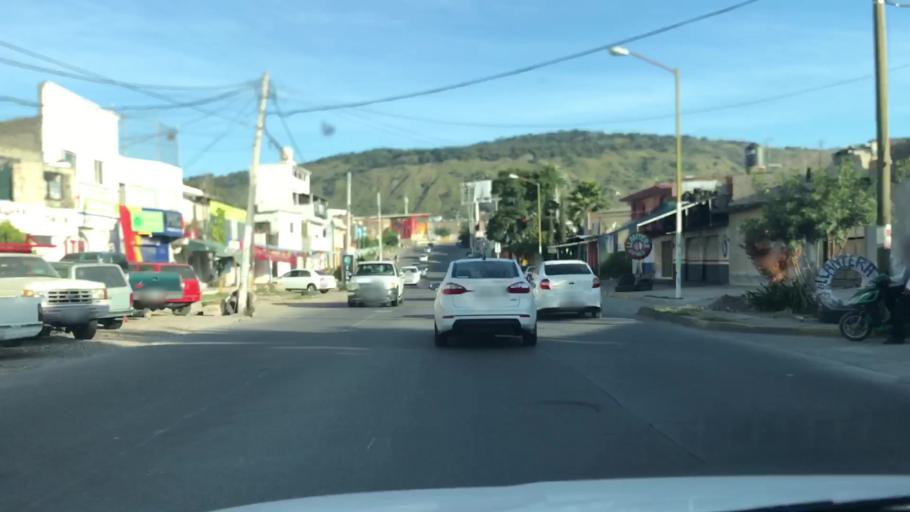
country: MX
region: Jalisco
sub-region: Tlajomulco de Zuniga
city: Palomar
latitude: 20.6382
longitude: -103.4604
